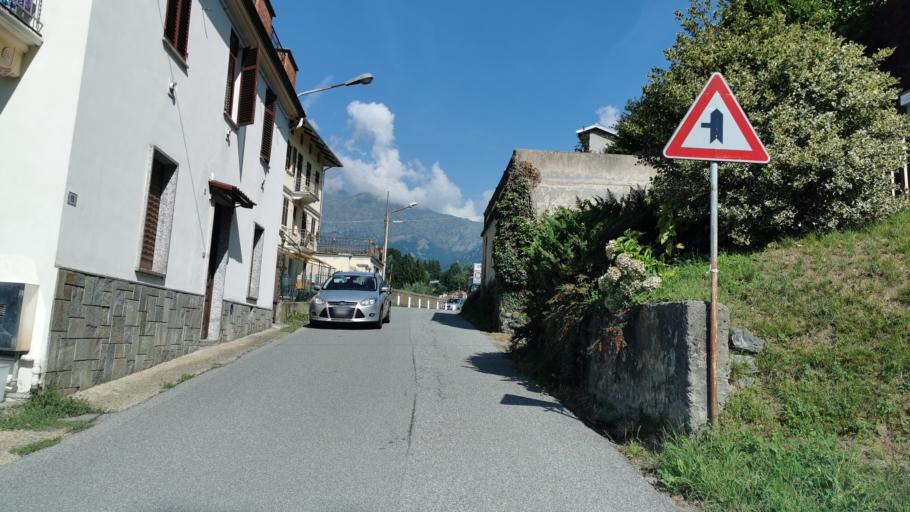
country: IT
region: Piedmont
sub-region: Provincia di Biella
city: Pollone
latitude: 45.5939
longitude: 8.0102
